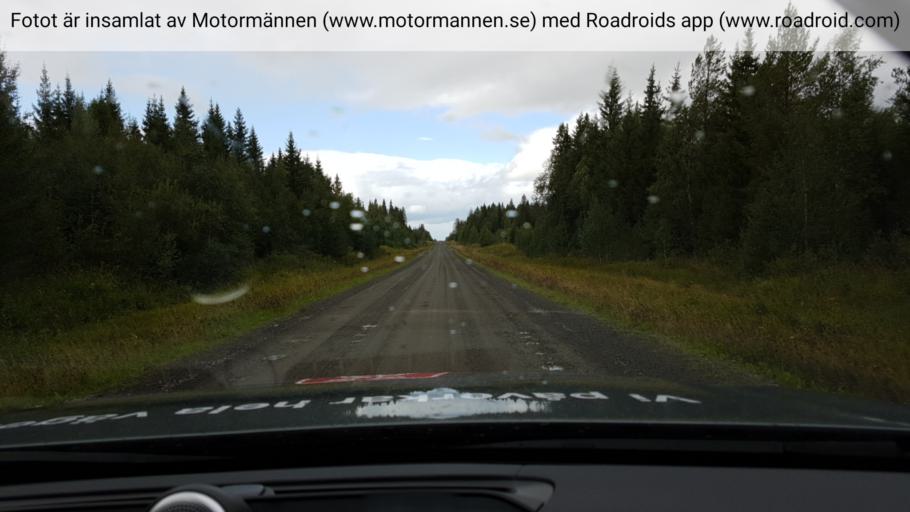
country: SE
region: Jaemtland
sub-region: OEstersunds Kommun
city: Lit
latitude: 63.6678
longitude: 14.8938
